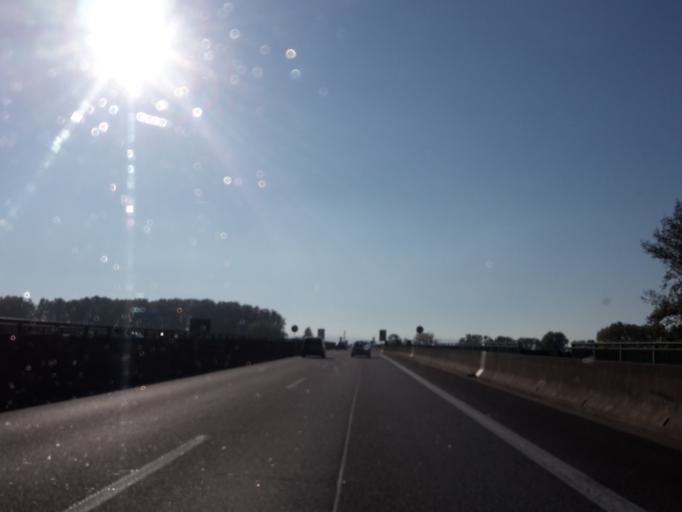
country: DE
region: Rheinland-Pfalz
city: Frankenthal
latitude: 49.5500
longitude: 8.4212
